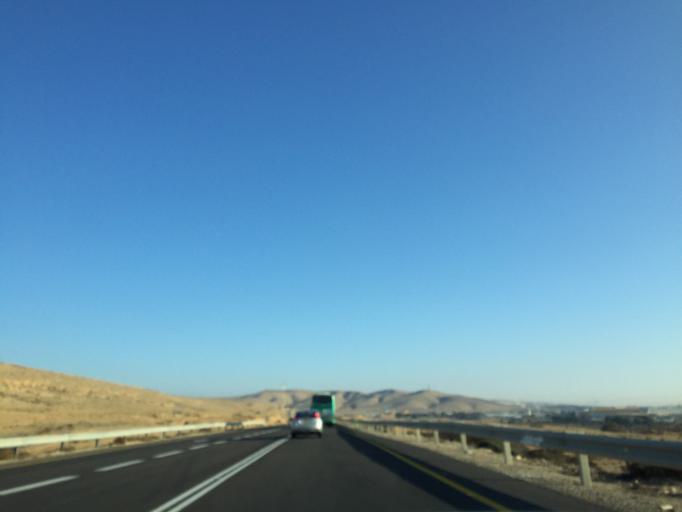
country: IL
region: Southern District
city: Dimona
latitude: 31.0561
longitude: 34.9990
